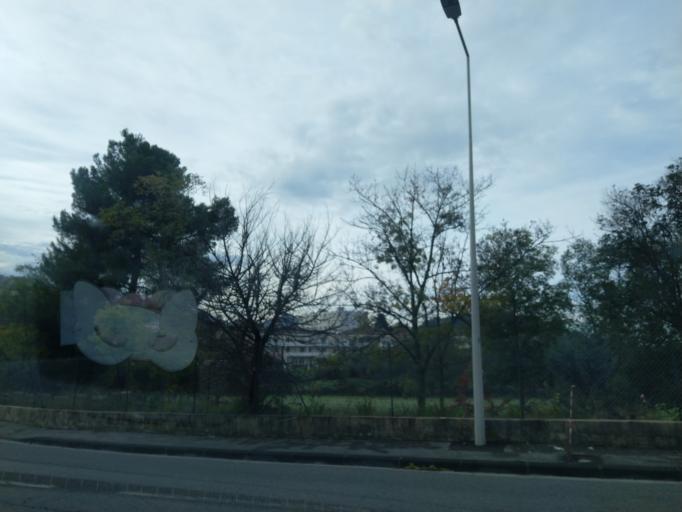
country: FR
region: Provence-Alpes-Cote d'Azur
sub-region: Departement des Bouches-du-Rhone
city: Marseille 11
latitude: 43.3014
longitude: 5.4577
